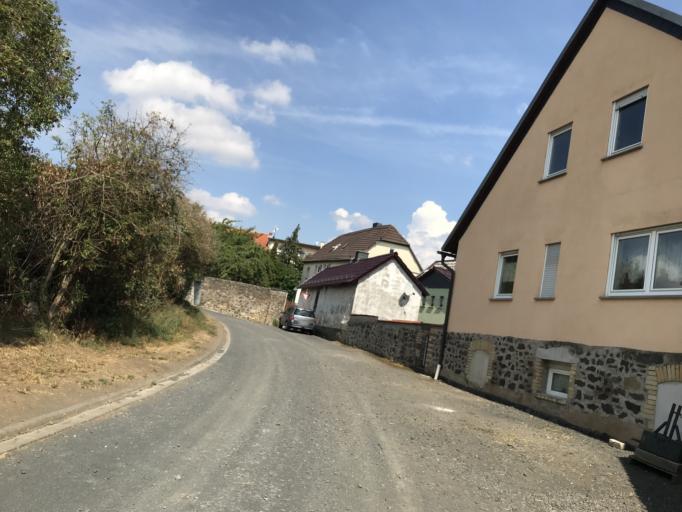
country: DE
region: Hesse
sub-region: Regierungsbezirk Darmstadt
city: Wolfersheim
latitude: 50.4395
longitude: 8.8295
